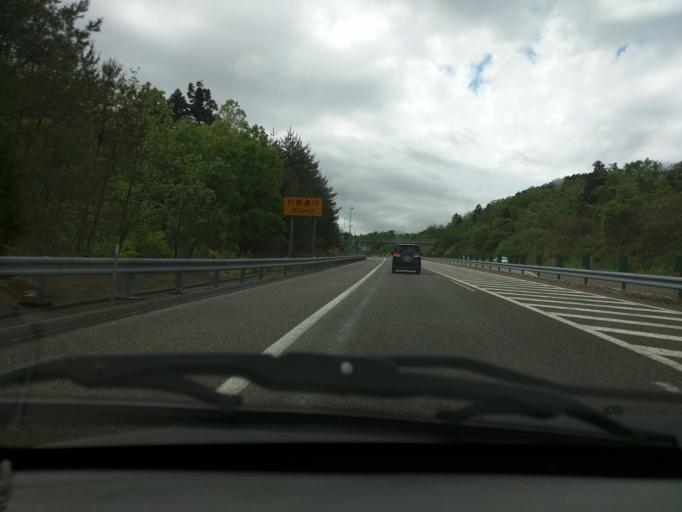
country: JP
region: Niigata
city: Joetsu
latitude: 37.1274
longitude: 138.2128
